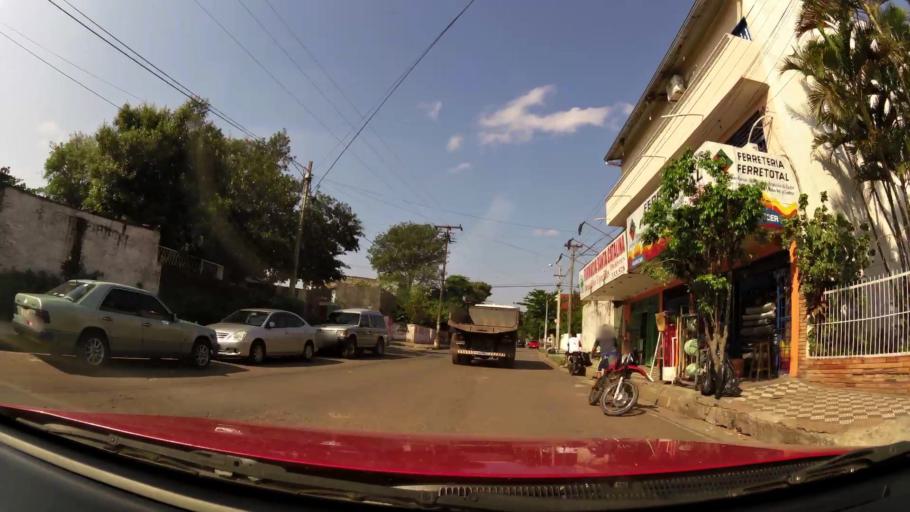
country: PY
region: Asuncion
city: Asuncion
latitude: -25.3202
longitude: -57.6397
